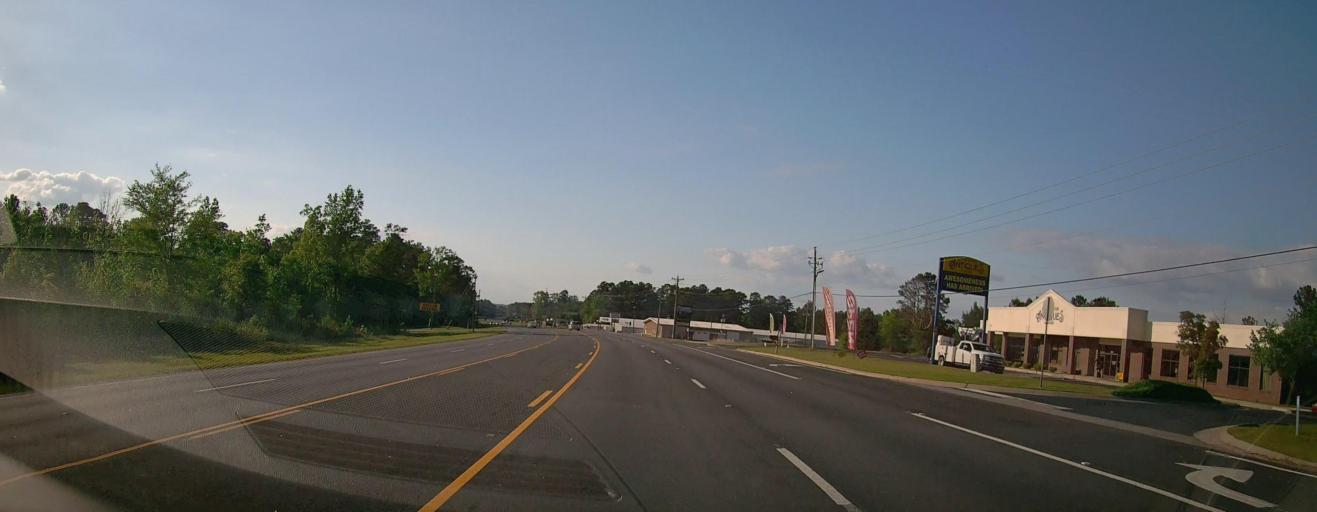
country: US
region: Georgia
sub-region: Baldwin County
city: Milledgeville
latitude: 33.1714
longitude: -83.2817
